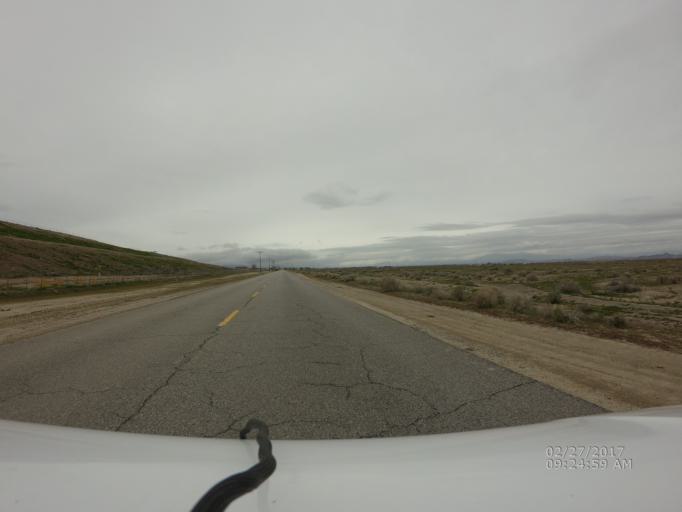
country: US
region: California
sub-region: Los Angeles County
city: Lancaster
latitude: 34.7481
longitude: -118.1164
